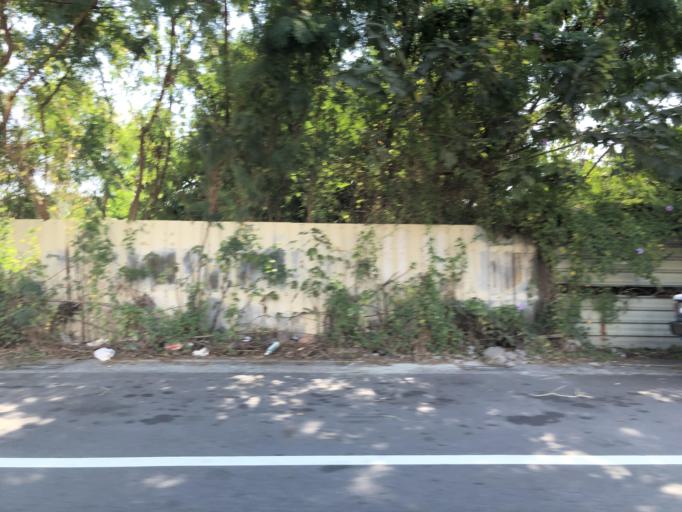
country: TW
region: Taiwan
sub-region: Tainan
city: Tainan
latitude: 23.0031
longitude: 120.2725
